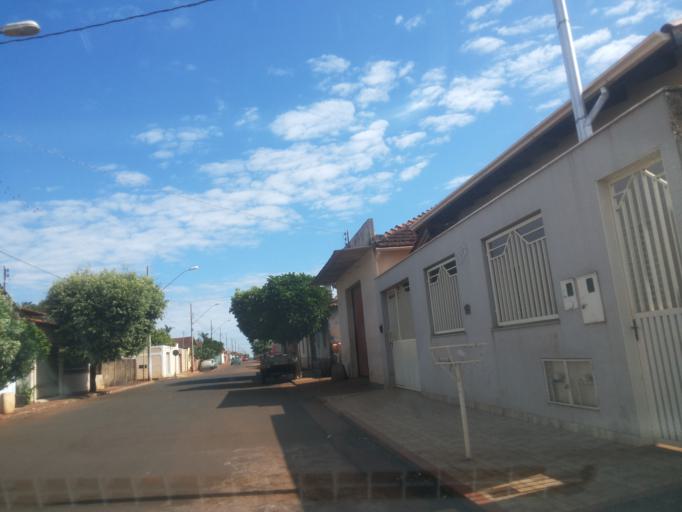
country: BR
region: Minas Gerais
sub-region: Centralina
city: Centralina
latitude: -18.5847
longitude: -49.1993
